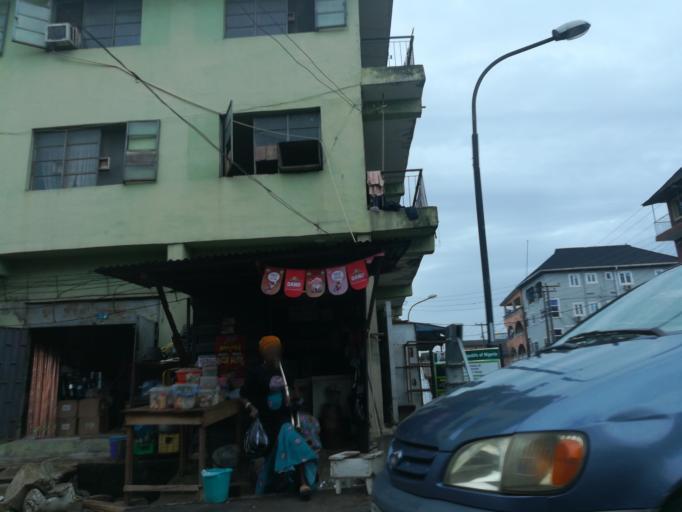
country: NG
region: Lagos
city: Ebute Metta
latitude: 6.4901
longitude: 3.3808
